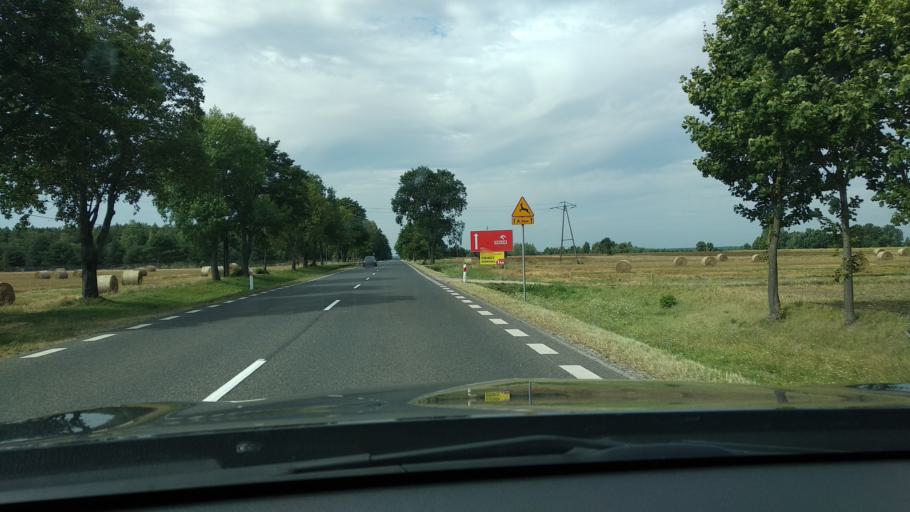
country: PL
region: Masovian Voivodeship
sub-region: Powiat pultuski
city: Zatory
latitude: 52.5483
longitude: 21.1785
